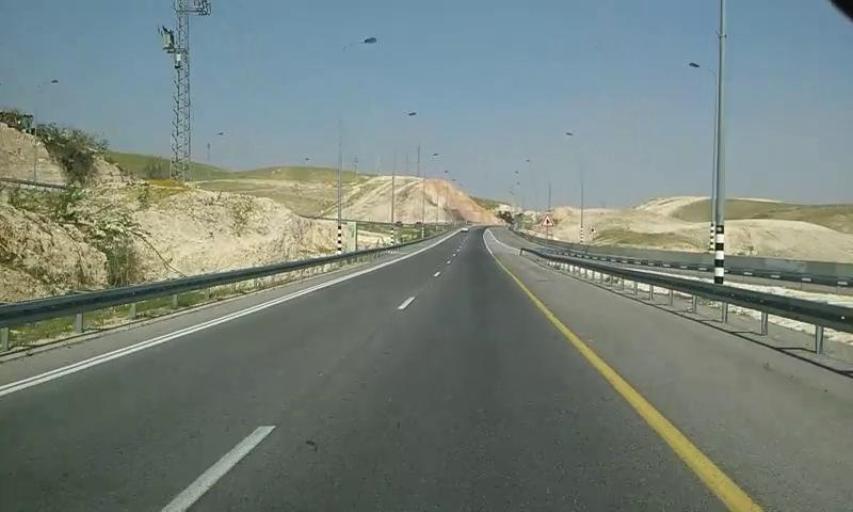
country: PS
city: Az Za`ayyim
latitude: 31.8108
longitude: 35.3401
